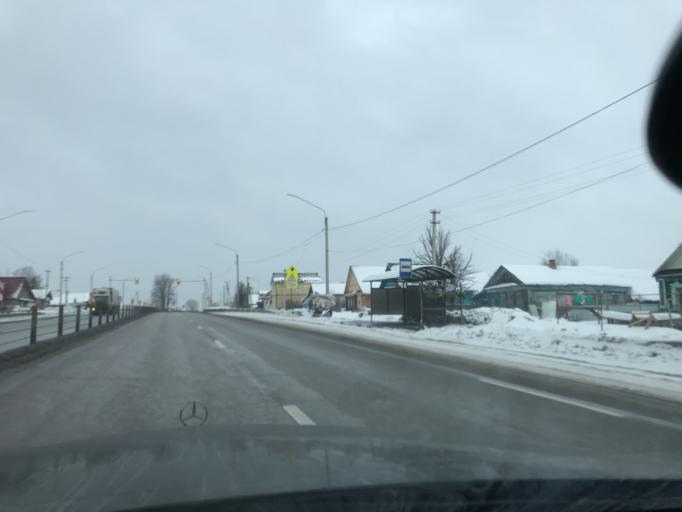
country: RU
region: Vladimir
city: Novovyazniki
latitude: 56.1721
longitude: 42.4236
